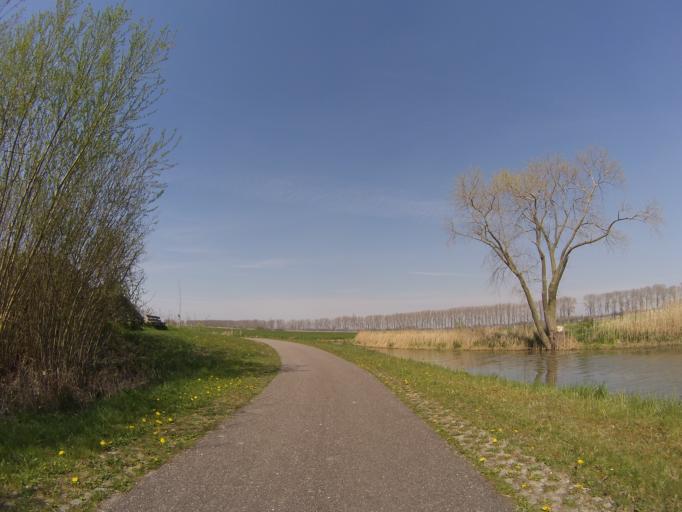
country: NL
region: Gelderland
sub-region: Gemeente Wageningen
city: Wageningen
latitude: 51.9738
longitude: 5.6258
